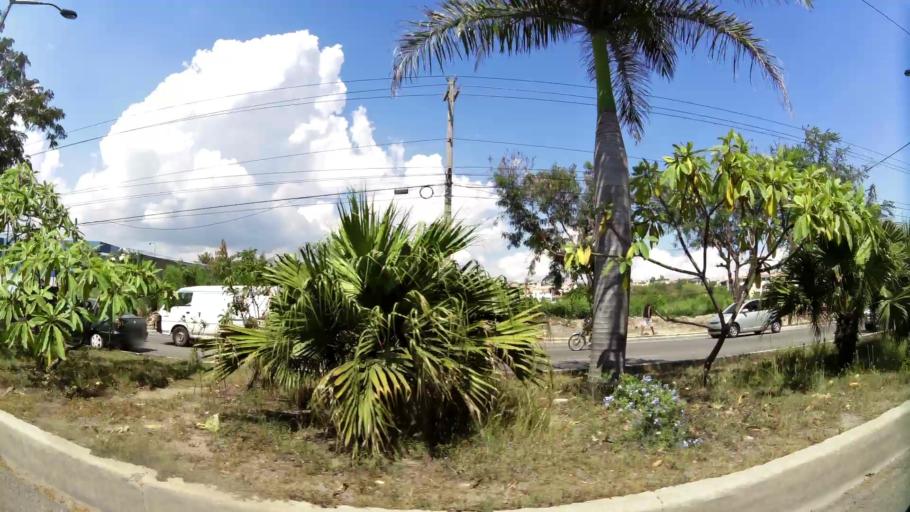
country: DO
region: Nacional
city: Bella Vista
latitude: 18.4590
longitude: -69.9852
